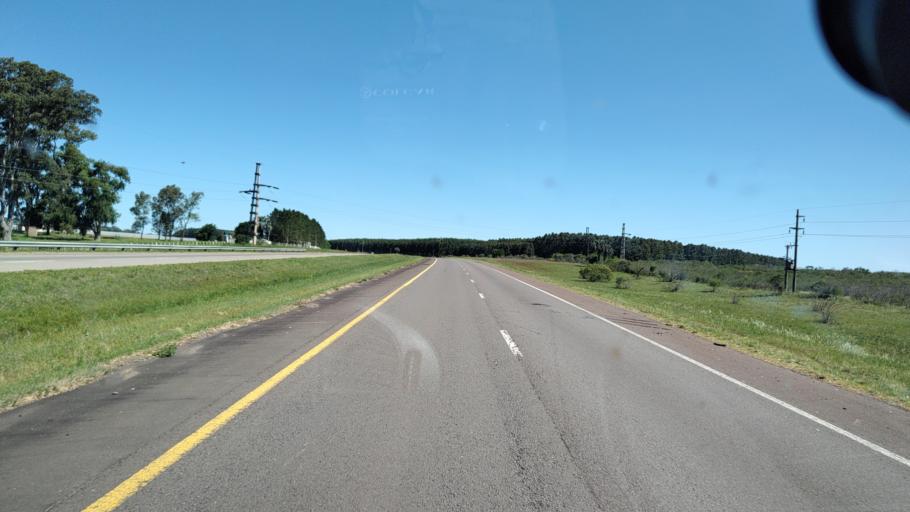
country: AR
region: Entre Rios
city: Ubajay
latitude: -31.9752
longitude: -58.3056
